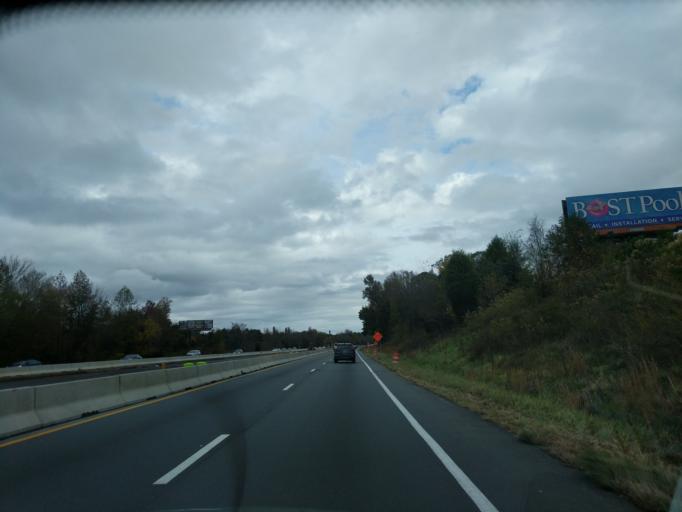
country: US
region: North Carolina
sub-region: Rowan County
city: China Grove
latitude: 35.5502
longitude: -80.5713
